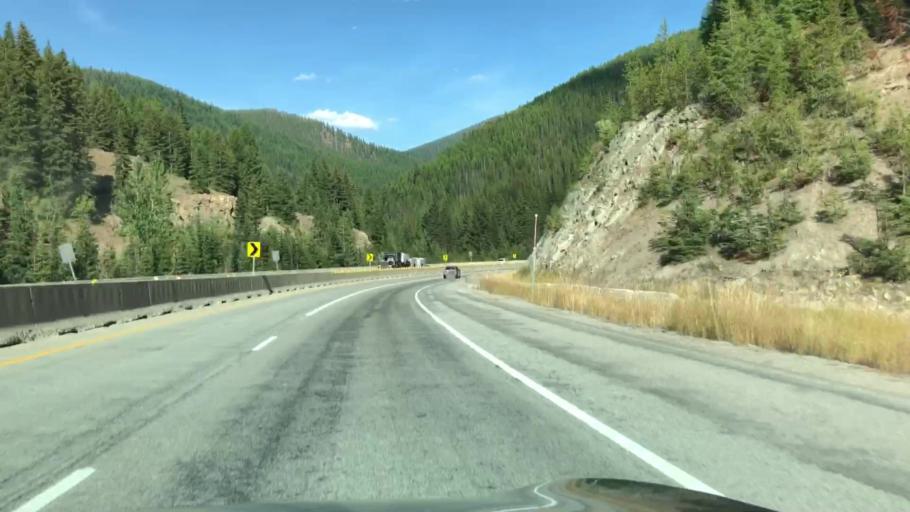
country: US
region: Idaho
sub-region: Shoshone County
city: Wallace
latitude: 47.4354
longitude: -115.6608
